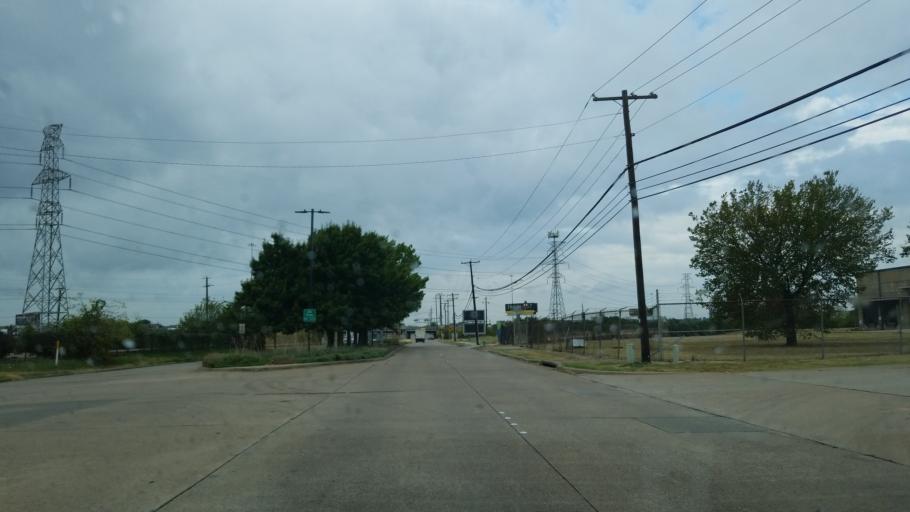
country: US
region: Texas
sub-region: Dallas County
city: Garland
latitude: 32.8788
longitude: -96.6843
